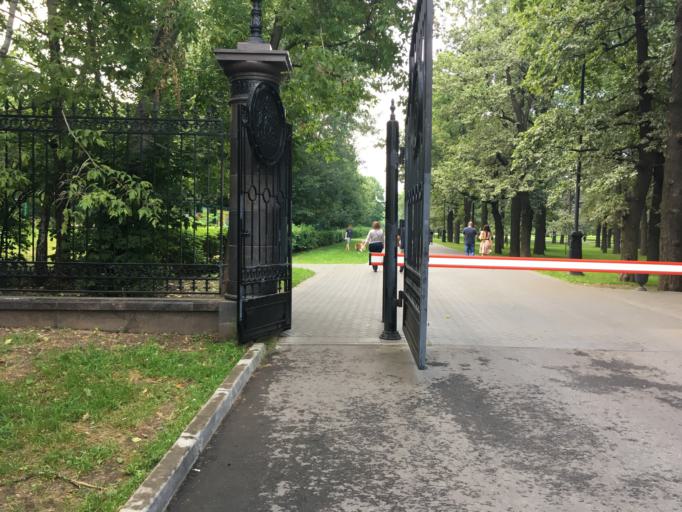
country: RU
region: Moscow
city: Ostankinskiy
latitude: 55.8240
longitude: 37.6095
